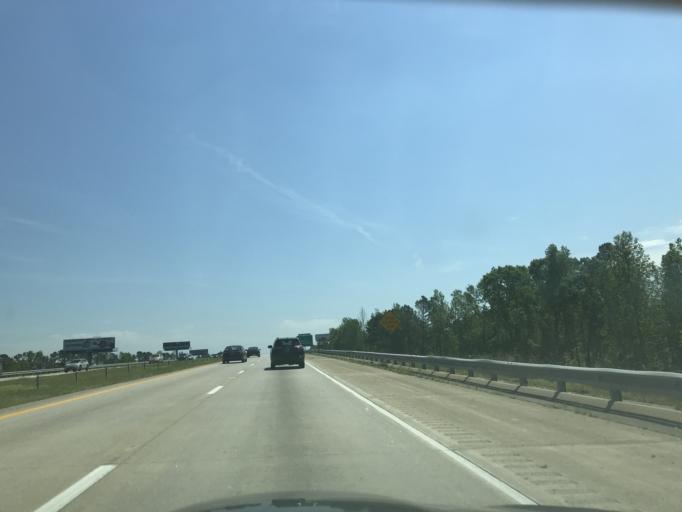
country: US
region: North Carolina
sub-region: Johnston County
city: Benson
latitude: 35.4106
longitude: -78.5245
